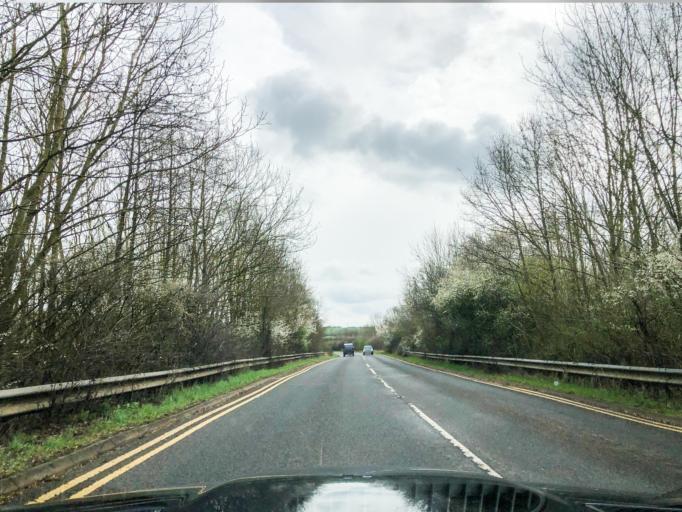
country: GB
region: England
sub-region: Warwickshire
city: Harbury
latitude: 52.1702
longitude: -1.4481
